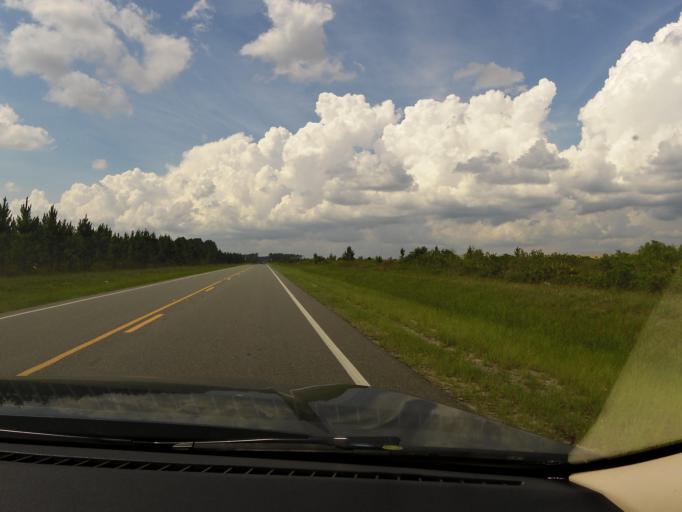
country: US
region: Florida
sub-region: Baker County
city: Macclenny
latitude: 30.2265
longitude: -82.0762
